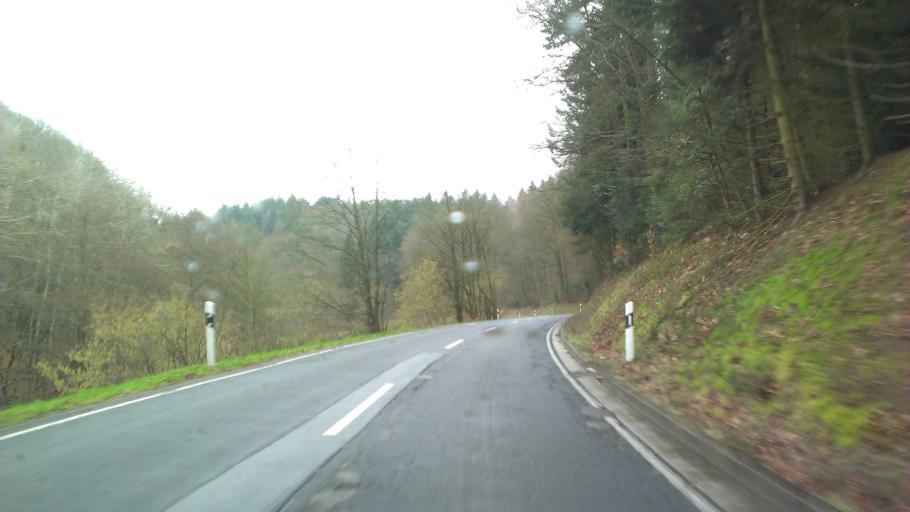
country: DE
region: Baden-Wuerttemberg
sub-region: Karlsruhe Region
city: Heiligkreuzsteinach
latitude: 49.4993
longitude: 8.7832
